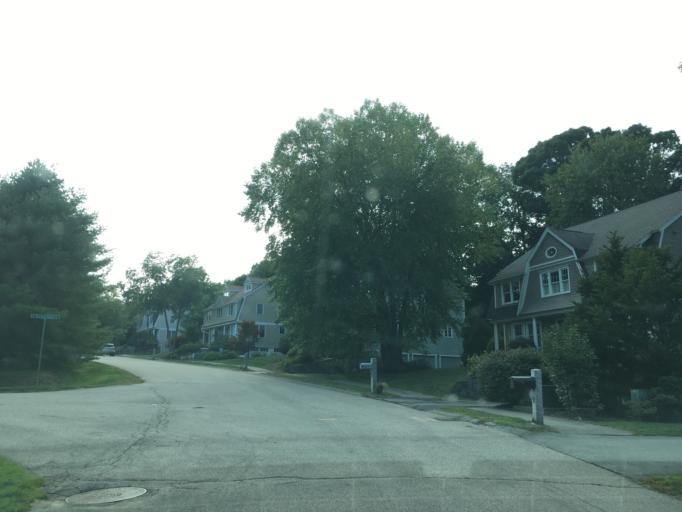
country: US
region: New Hampshire
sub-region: Rockingham County
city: Exeter
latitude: 42.9805
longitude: -70.9259
